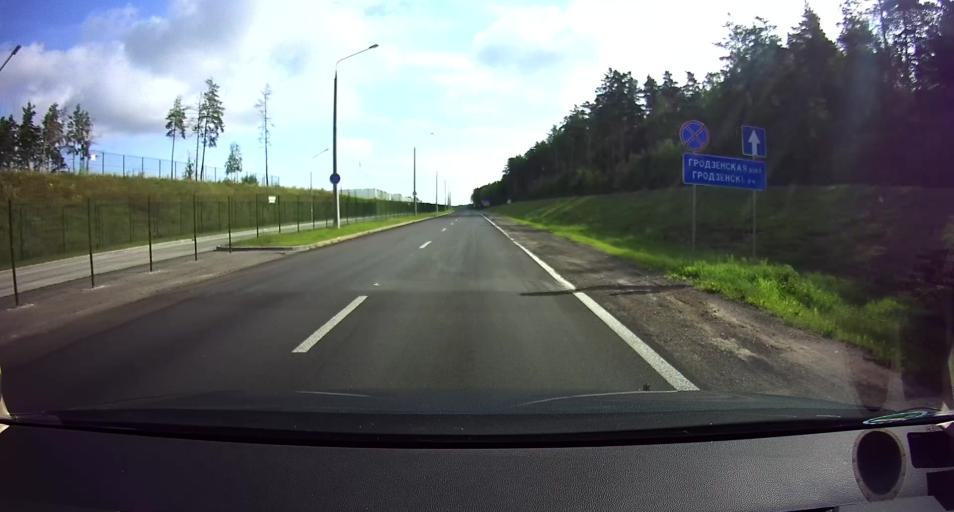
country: PL
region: Podlasie
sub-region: Powiat sokolski
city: Kuznica
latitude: 53.5246
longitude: 23.6711
